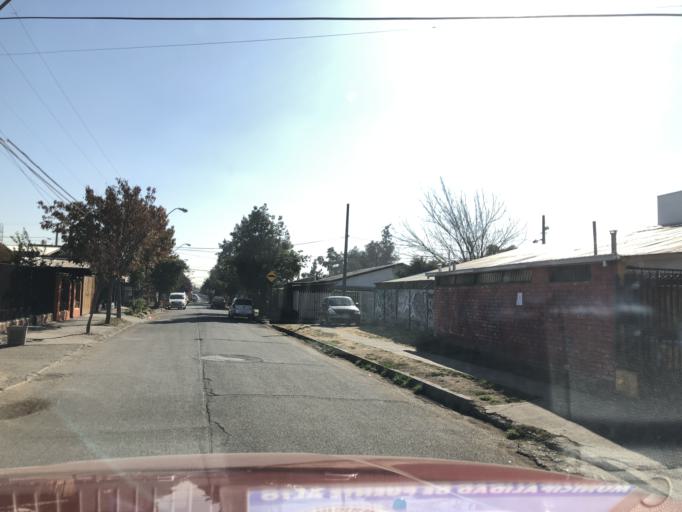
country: CL
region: Santiago Metropolitan
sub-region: Provincia de Cordillera
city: Puente Alto
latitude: -33.5725
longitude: -70.5746
